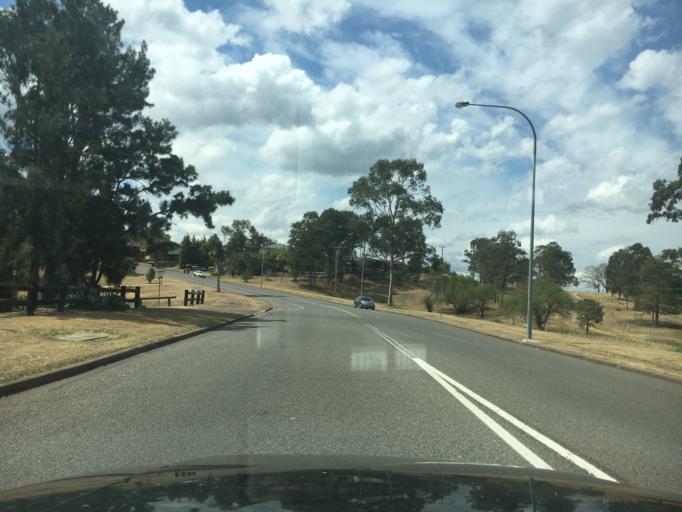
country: AU
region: New South Wales
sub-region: Singleton
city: Singleton
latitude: -32.5480
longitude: 151.1692
